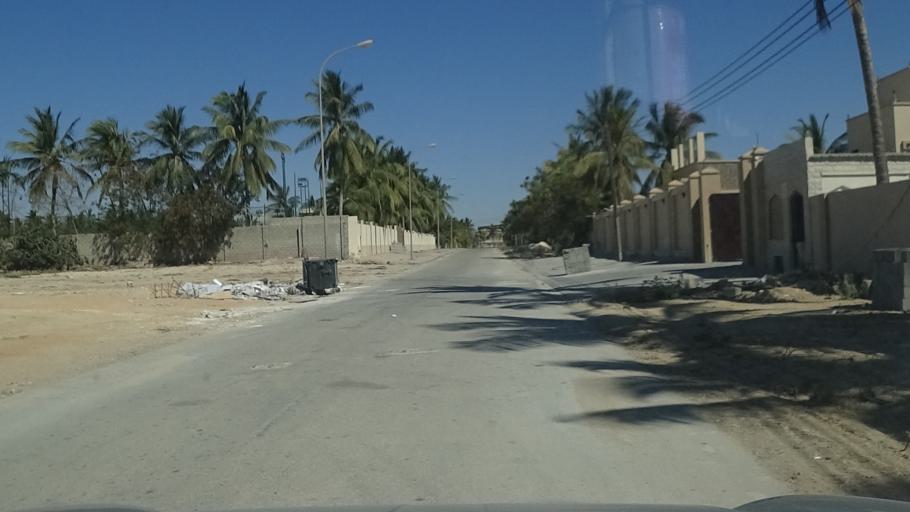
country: OM
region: Zufar
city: Salalah
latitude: 17.0269
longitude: 54.1625
